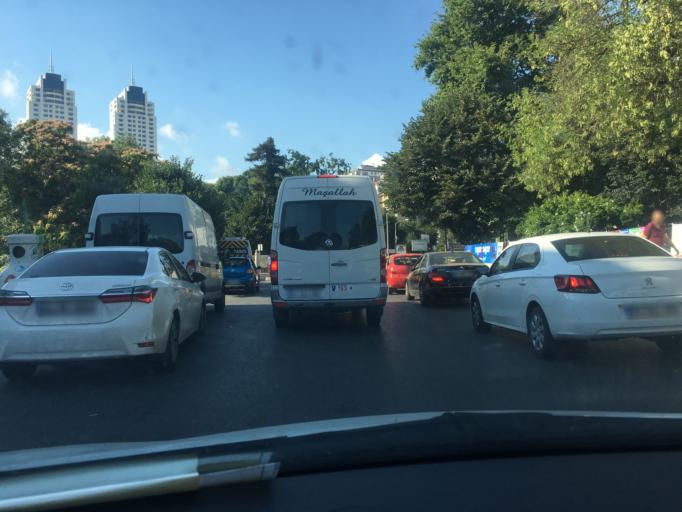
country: TR
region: Istanbul
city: Sisli
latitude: 41.0498
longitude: 29.0021
